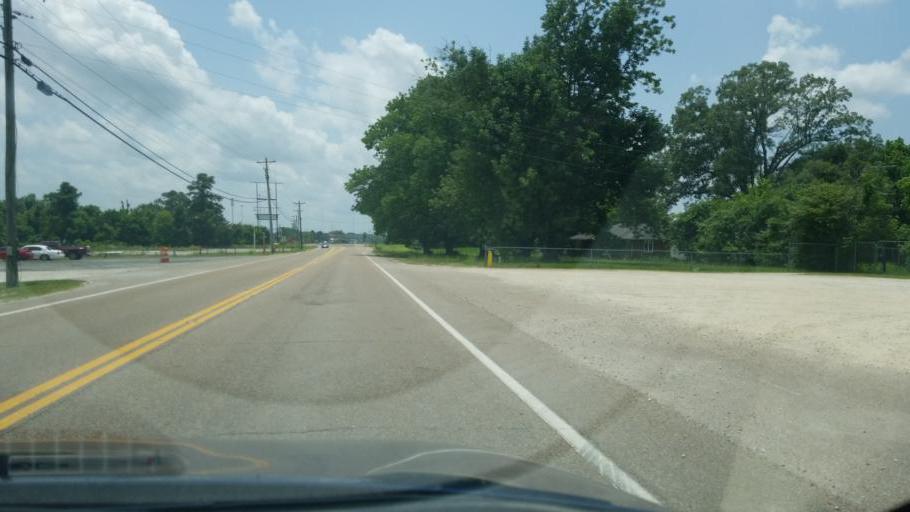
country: US
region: Tennessee
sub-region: Madison County
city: Jackson
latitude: 35.6855
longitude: -88.7389
